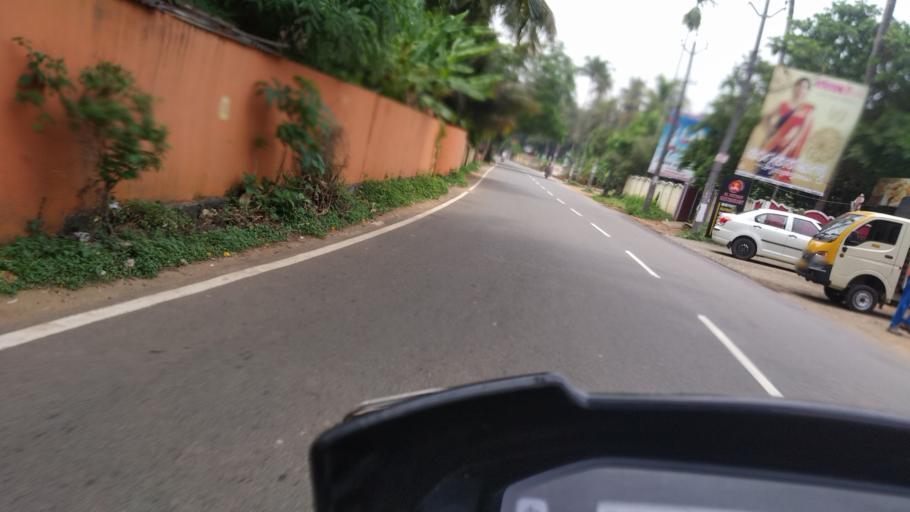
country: IN
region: Kerala
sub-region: Ernakulam
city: Aluva
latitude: 10.1559
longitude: 76.3205
